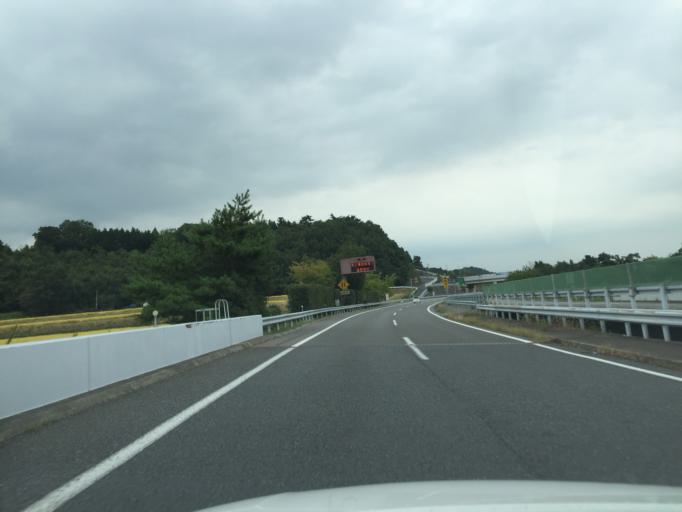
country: JP
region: Fukushima
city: Iwaki
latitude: 37.0619
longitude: 140.8324
